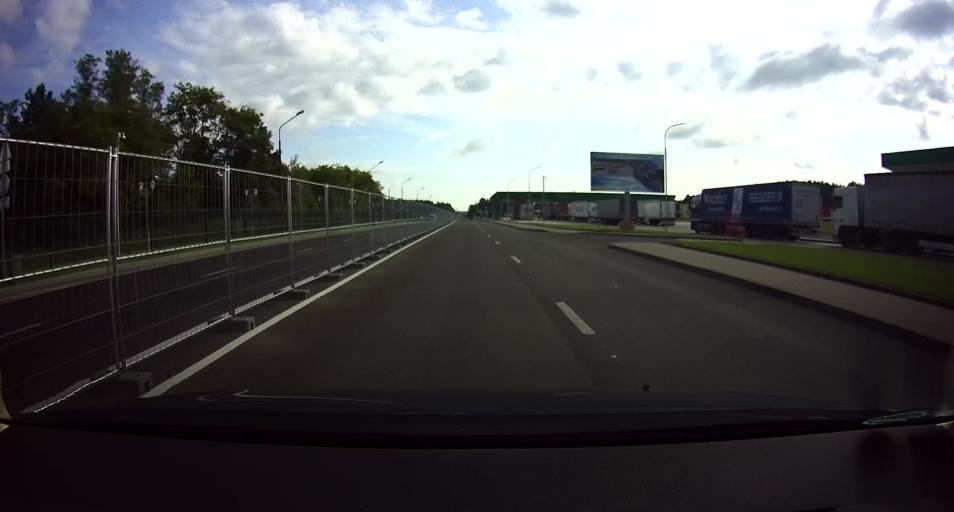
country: PL
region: Podlasie
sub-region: Powiat sokolski
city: Kuznica
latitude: 53.5222
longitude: 23.6613
